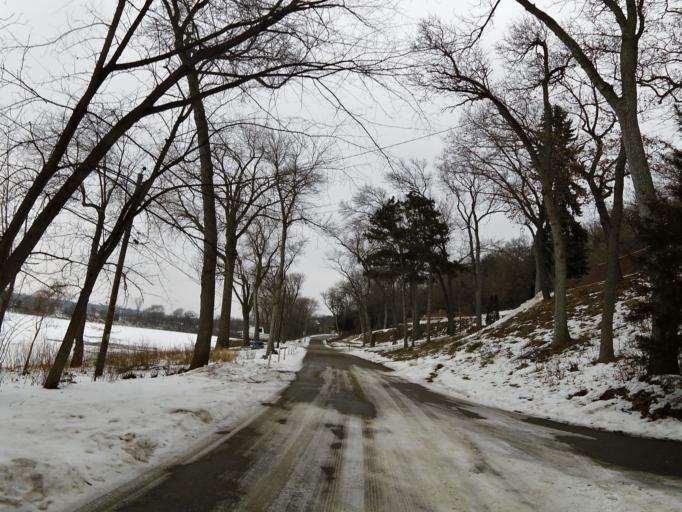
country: US
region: Minnesota
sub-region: Washington County
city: Lakeland
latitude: 44.9595
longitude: -92.7490
